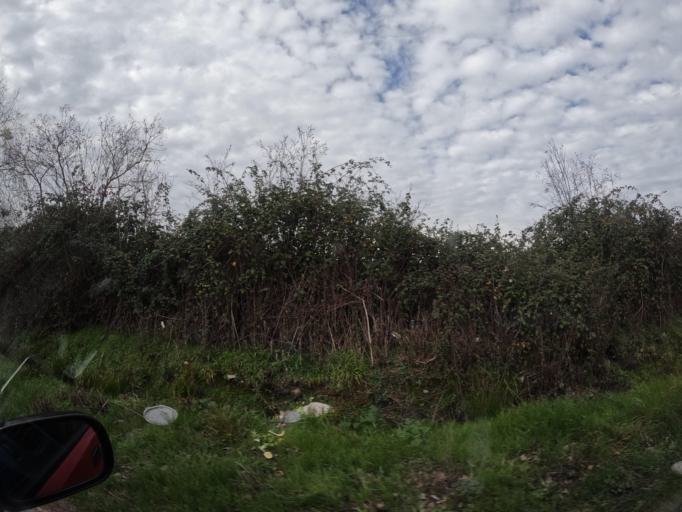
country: CL
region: Maule
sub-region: Provincia de Linares
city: Linares
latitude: -35.8617
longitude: -71.6170
